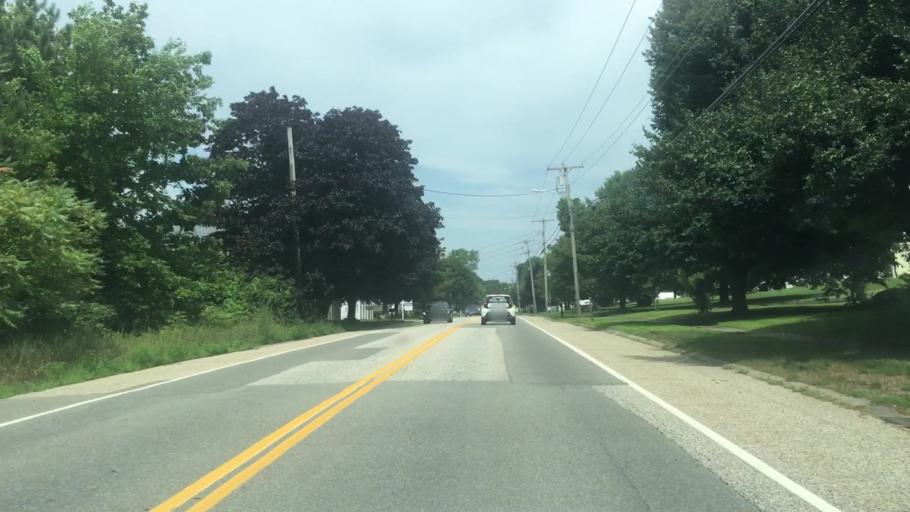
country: US
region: Maine
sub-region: Cumberland County
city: South Portland Gardens
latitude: 43.6127
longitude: -70.2794
